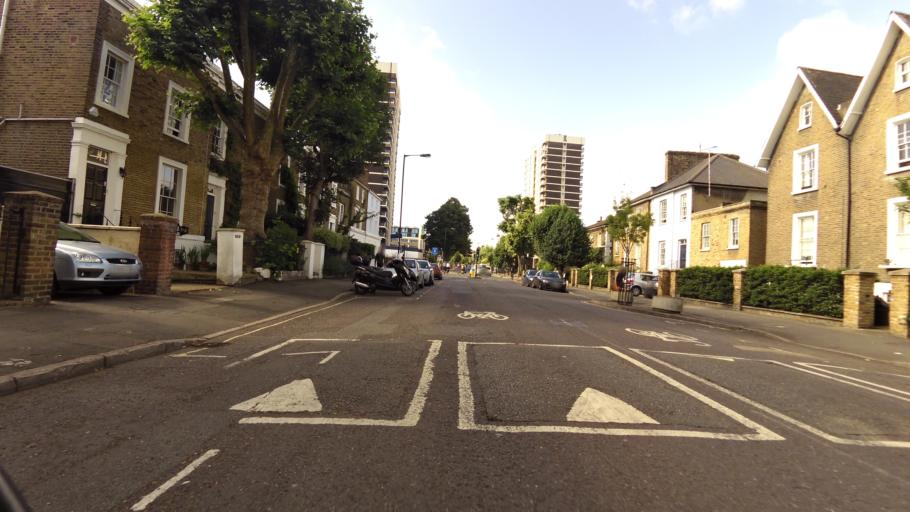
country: GB
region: England
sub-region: Greater London
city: Islington
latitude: 51.5399
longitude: -0.0809
